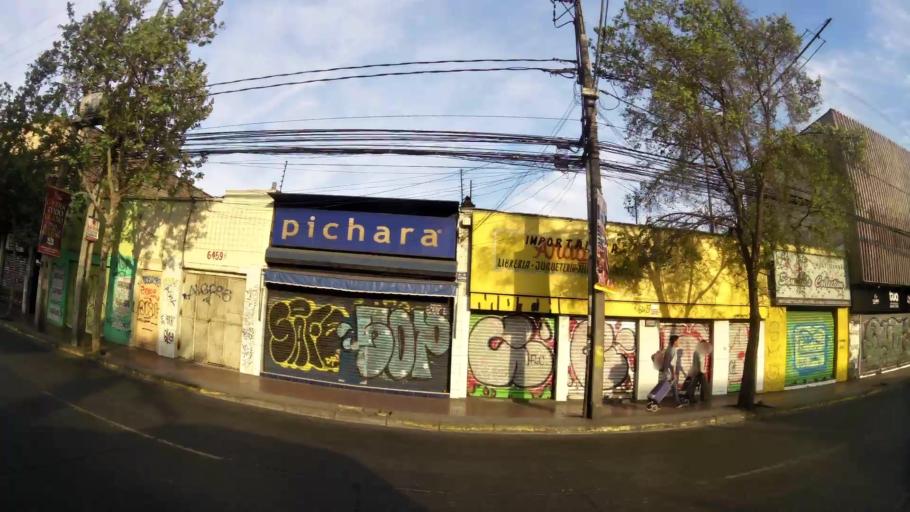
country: CL
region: Santiago Metropolitan
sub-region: Provincia de Santiago
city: Santiago
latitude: -33.5159
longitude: -70.6586
